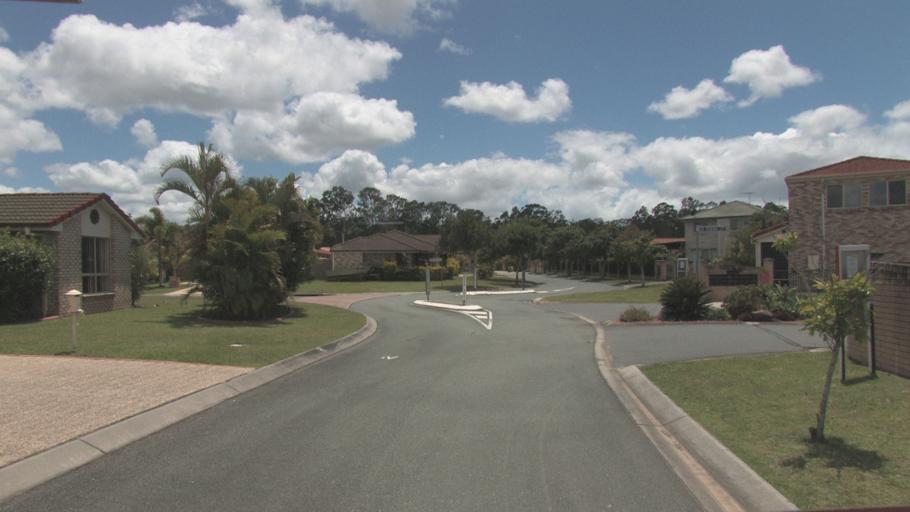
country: AU
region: Queensland
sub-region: Logan
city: Beenleigh
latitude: -27.6750
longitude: 153.2130
